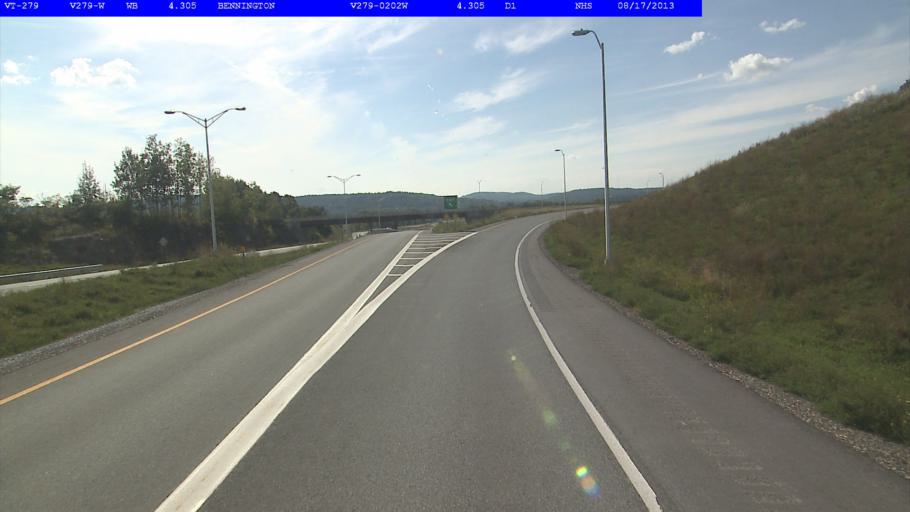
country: US
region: Vermont
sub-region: Bennington County
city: Bennington
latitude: 42.9022
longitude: -73.1971
